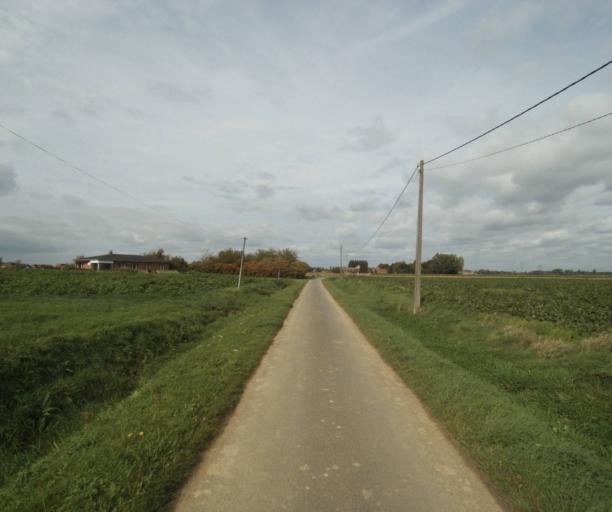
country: FR
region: Nord-Pas-de-Calais
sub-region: Departement du Nord
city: Bois-Grenier
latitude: 50.6359
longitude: 2.8840
